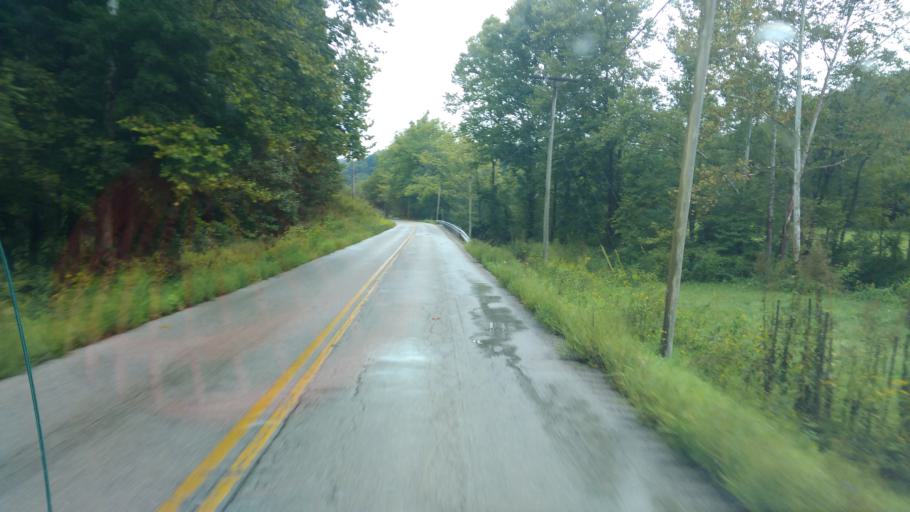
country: US
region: Kentucky
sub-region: Fleming County
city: Flemingsburg
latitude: 38.4448
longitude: -83.4987
